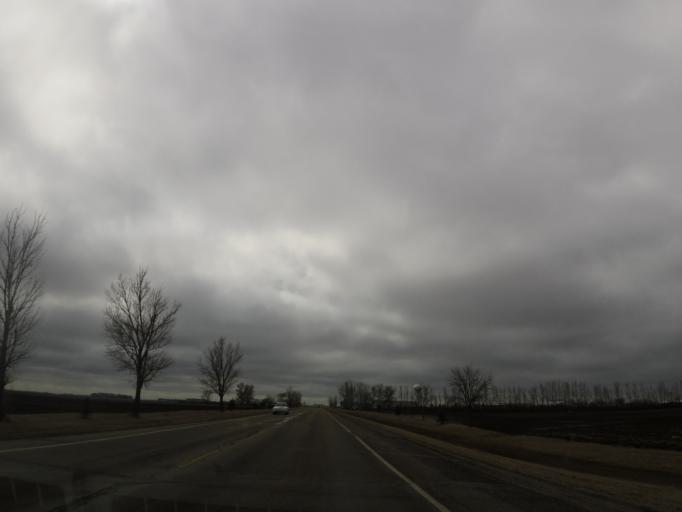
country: US
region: North Dakota
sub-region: Cass County
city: Casselton
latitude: 46.8863
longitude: -97.2107
